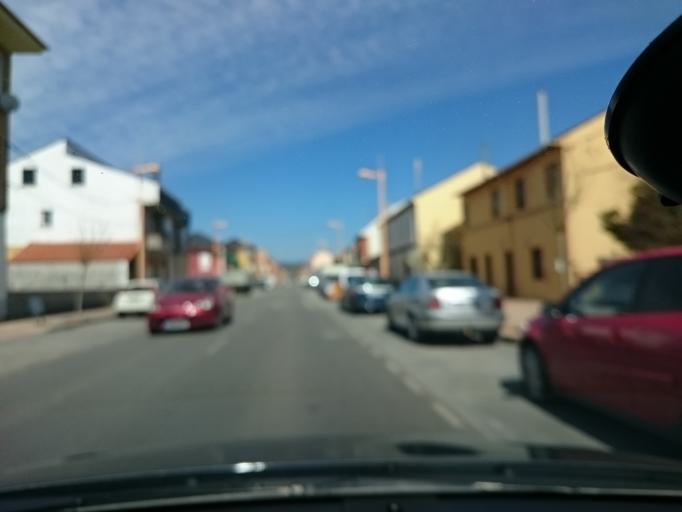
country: ES
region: Castille and Leon
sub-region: Provincia de Leon
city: Camponaraya
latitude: 42.5685
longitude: -6.6394
